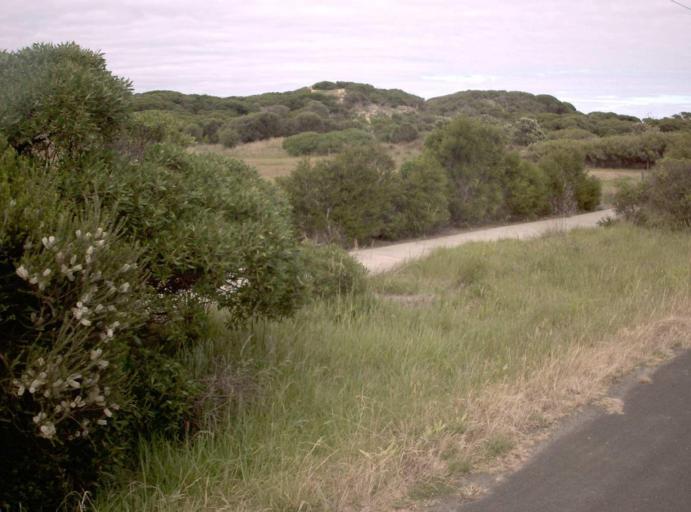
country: AU
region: Victoria
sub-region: Bass Coast
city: Phillip Island
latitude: -38.5146
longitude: 145.3088
